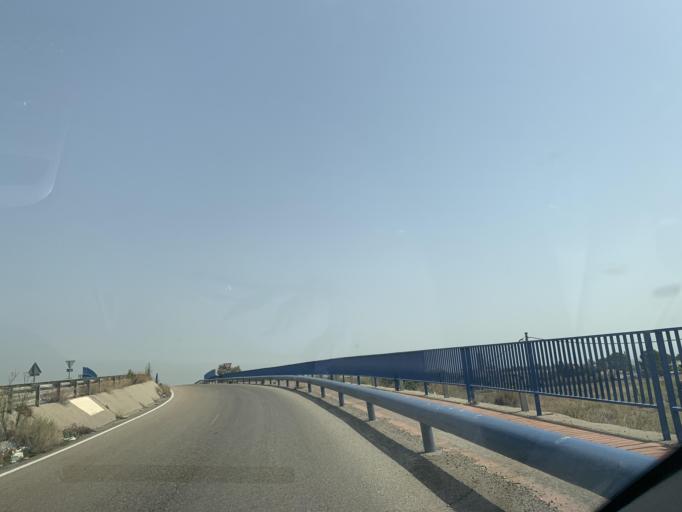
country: ES
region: Aragon
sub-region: Provincia de Zaragoza
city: Zaragoza
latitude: 41.6029
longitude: -0.8302
